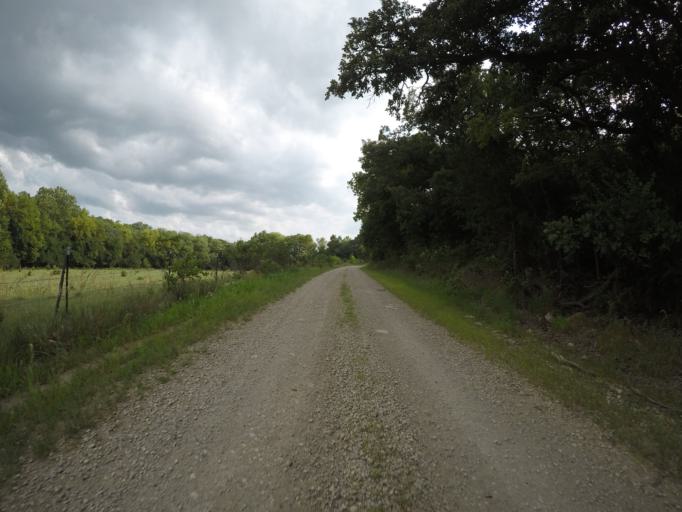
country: US
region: Kansas
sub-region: Marshall County
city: Blue Rapids
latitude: 39.5107
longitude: -96.8324
